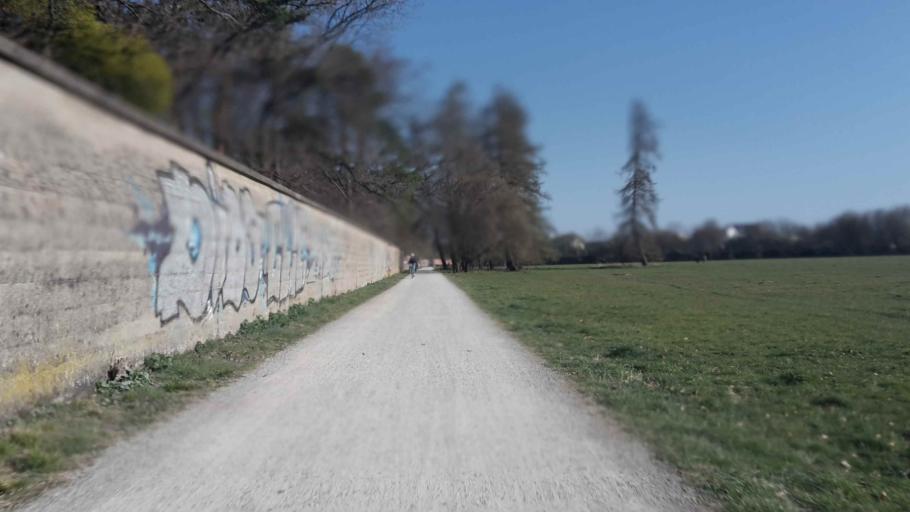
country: DE
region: Bavaria
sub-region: Upper Bavaria
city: Pasing
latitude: 48.1506
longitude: 11.4920
